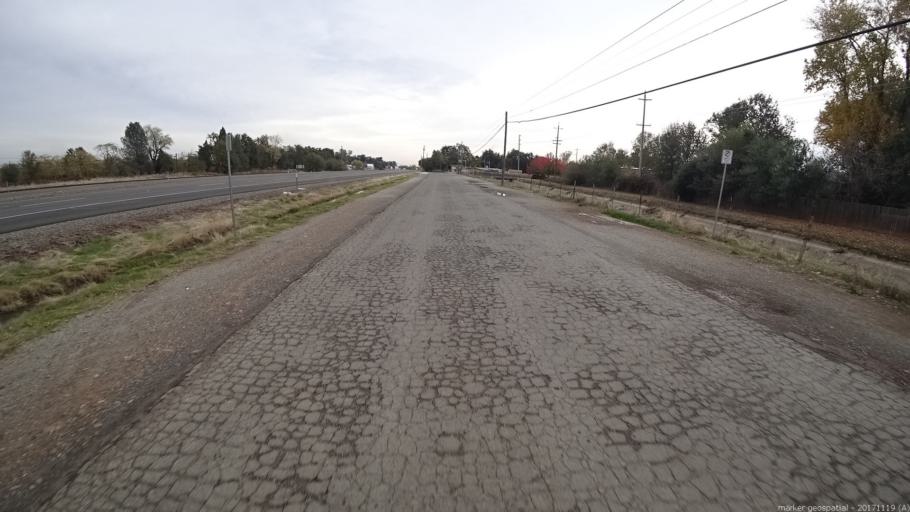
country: US
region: California
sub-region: Shasta County
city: Anderson
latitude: 40.4936
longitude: -122.3651
